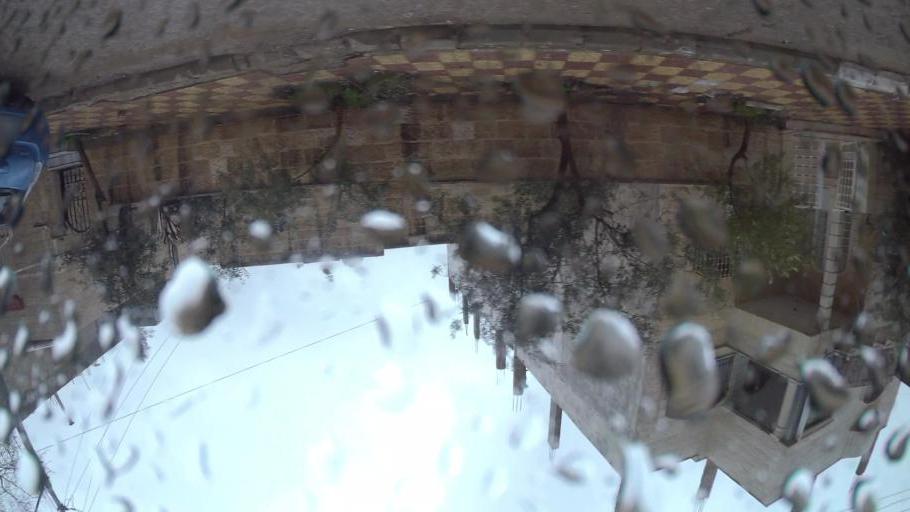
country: JO
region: Amman
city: Al Jubayhah
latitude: 32.0477
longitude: 35.8808
